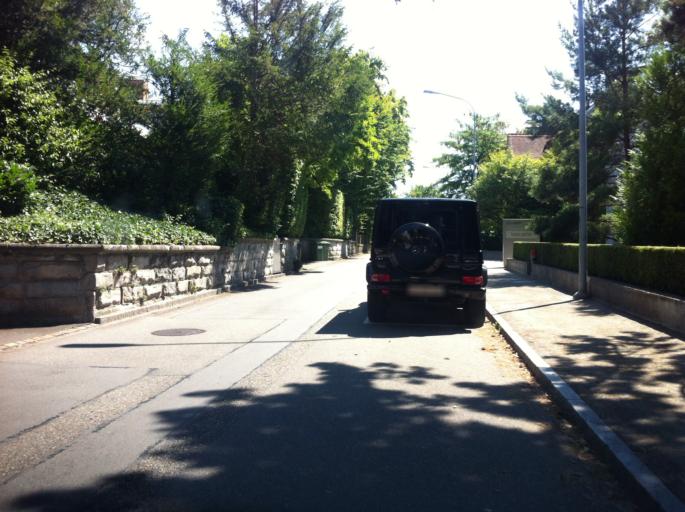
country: CH
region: Zurich
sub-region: Bezirk Meilen
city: Zollikon
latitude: 47.3419
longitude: 8.5715
